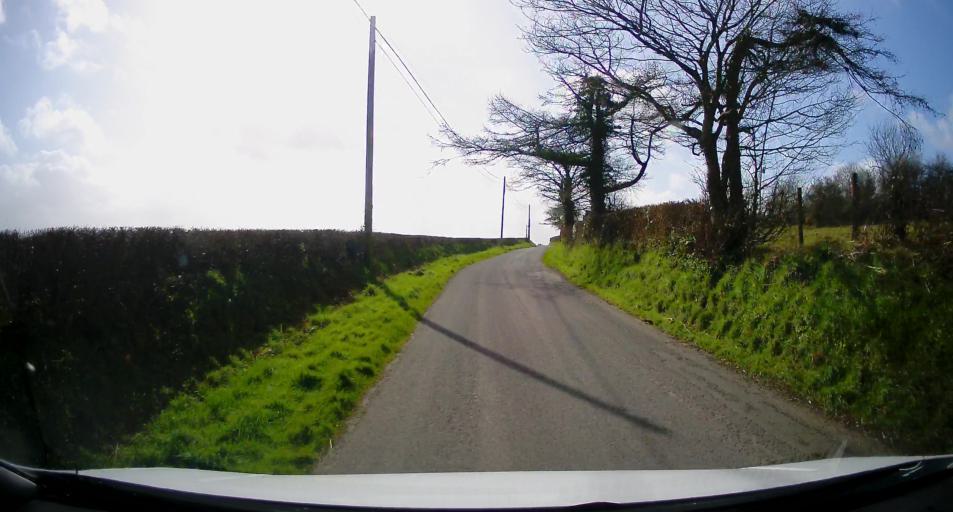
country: GB
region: Wales
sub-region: County of Ceredigion
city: Aberporth
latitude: 52.0790
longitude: -4.5444
